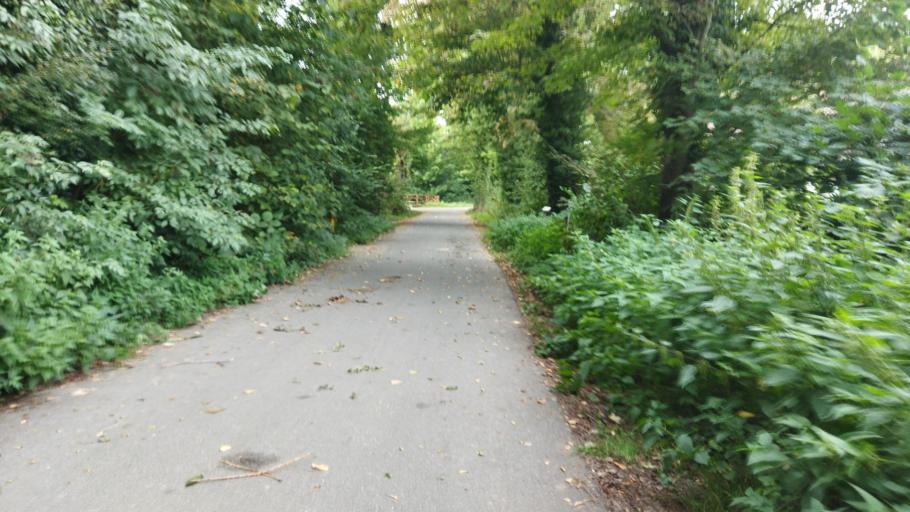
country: DE
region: North Rhine-Westphalia
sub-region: Regierungsbezirk Munster
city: Telgte
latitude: 52.0165
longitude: 7.7618
